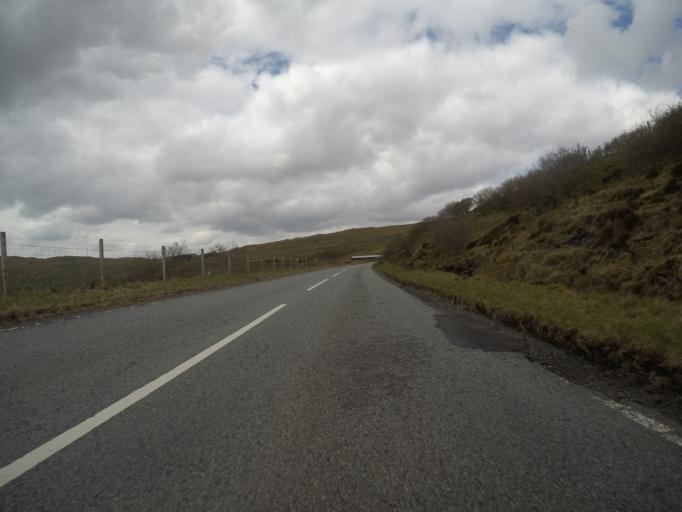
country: GB
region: Scotland
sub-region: Highland
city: Isle of Skye
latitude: 57.3262
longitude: -6.3331
